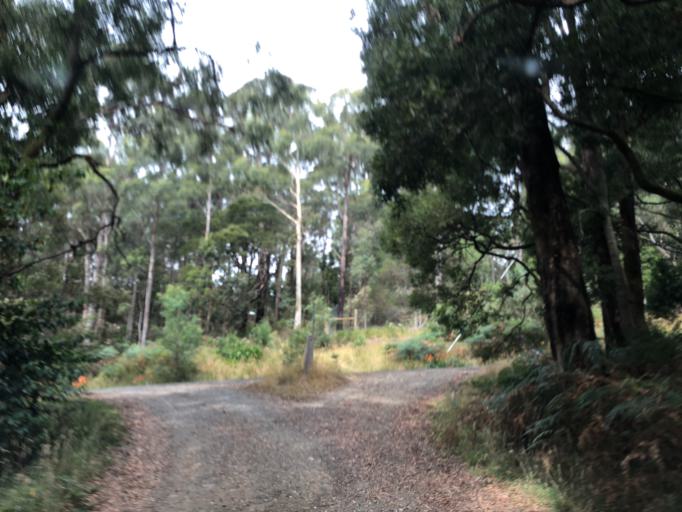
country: AU
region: Victoria
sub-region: Moorabool
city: Bacchus Marsh
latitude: -37.4763
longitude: 144.2903
